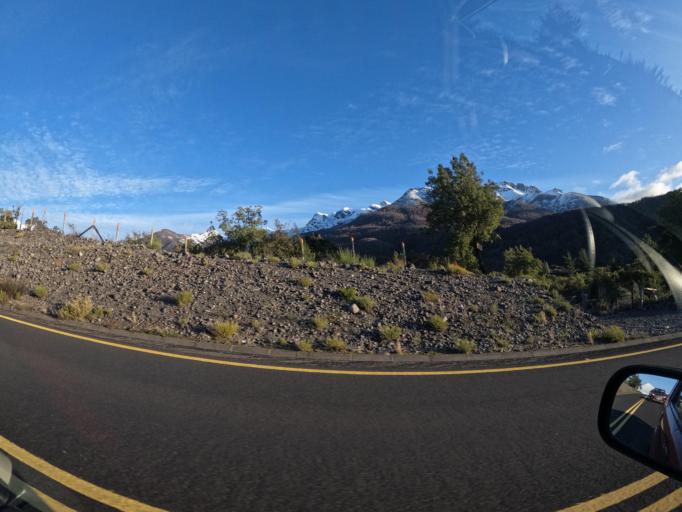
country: CL
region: Biobio
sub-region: Provincia de Biobio
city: Mulchen
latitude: -37.3429
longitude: -71.5925
